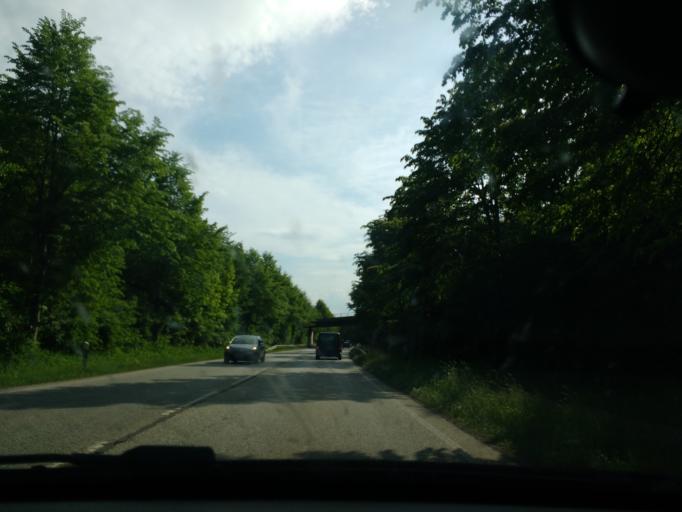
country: DE
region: Schleswig-Holstein
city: Einhaus
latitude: 53.7265
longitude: 10.7371
